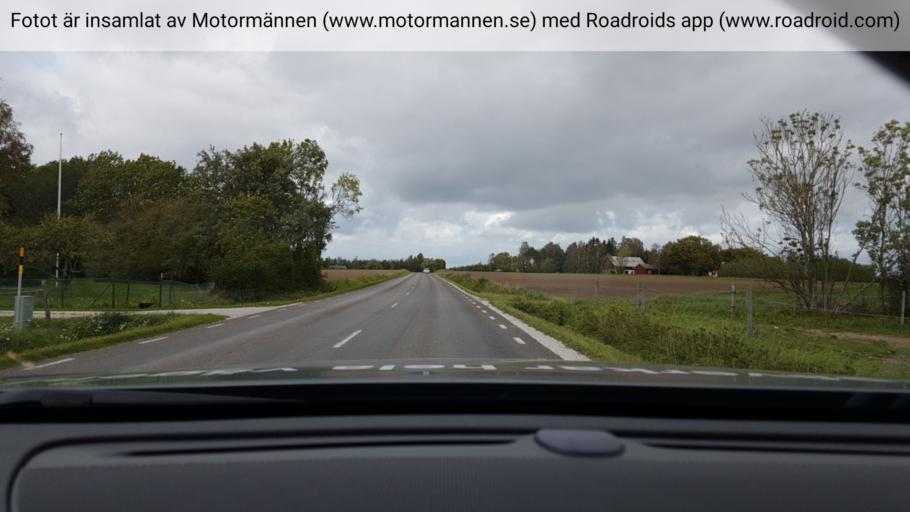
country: SE
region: Gotland
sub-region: Gotland
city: Klintehamn
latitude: 57.4623
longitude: 18.3573
